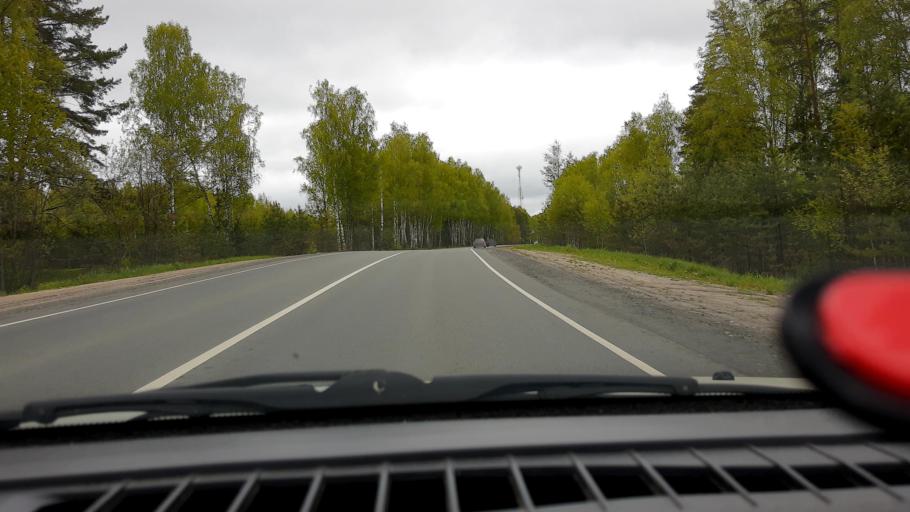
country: RU
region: Nizjnij Novgorod
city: Linda
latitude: 56.7035
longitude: 44.2185
